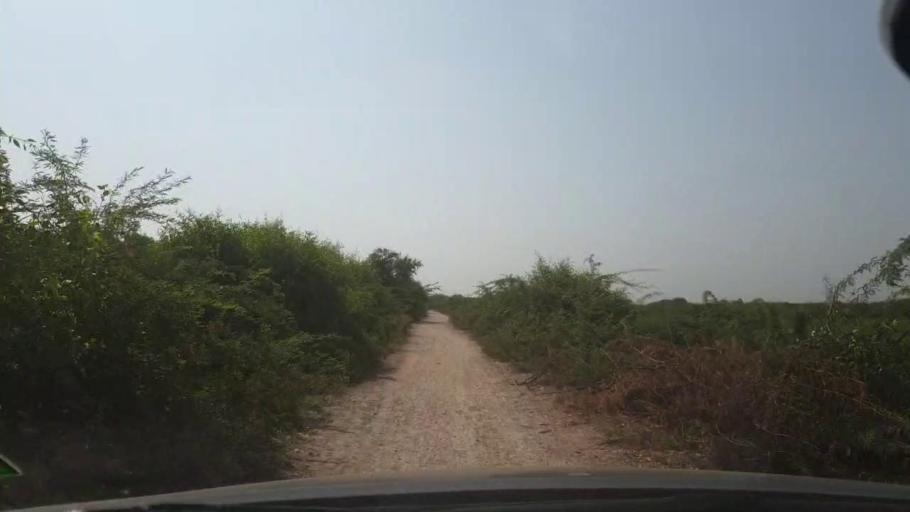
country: PK
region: Sindh
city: Naukot
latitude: 24.7959
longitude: 69.2434
